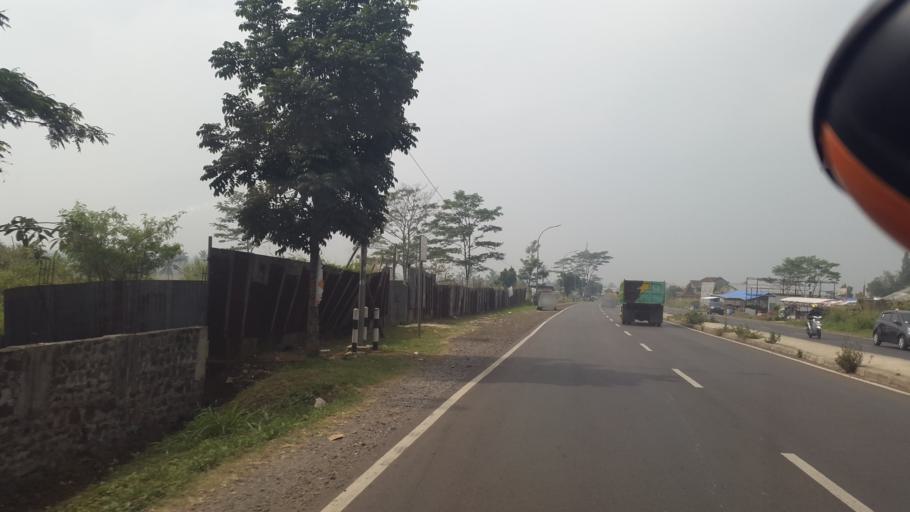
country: ID
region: West Java
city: Sukabumi
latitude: -6.9217
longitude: 106.8909
